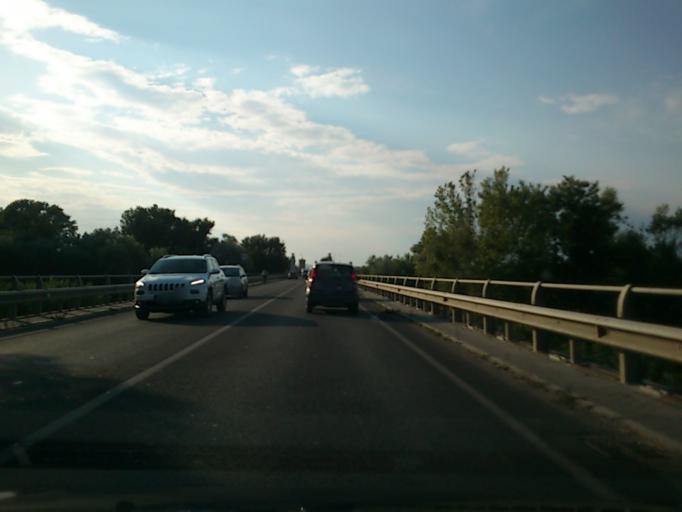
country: IT
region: The Marches
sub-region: Provincia di Pesaro e Urbino
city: Fano
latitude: 43.8266
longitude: 13.0535
